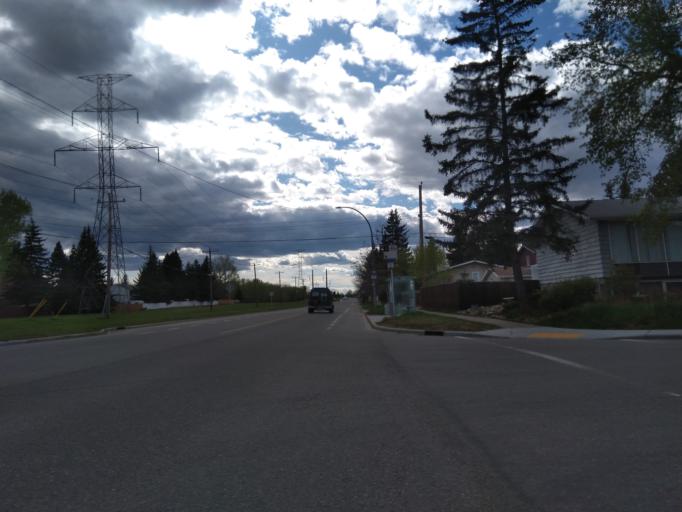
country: CA
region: Alberta
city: Calgary
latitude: 50.9946
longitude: -114.1318
